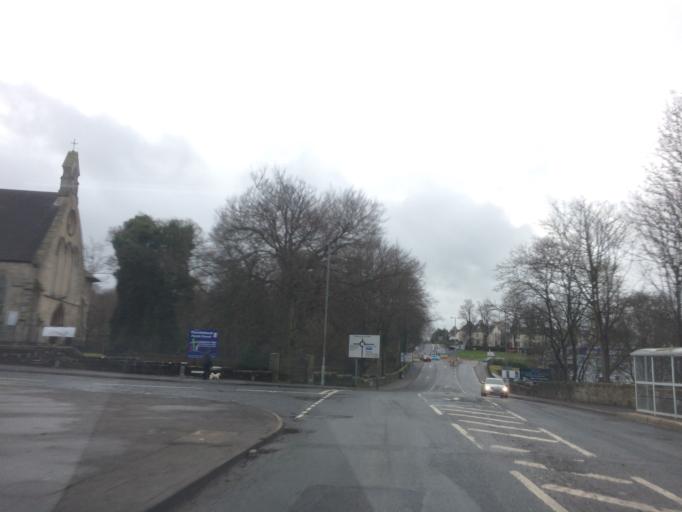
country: GB
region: Scotland
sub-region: East Renfrewshire
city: Giffnock
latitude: 55.8017
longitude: -4.3209
